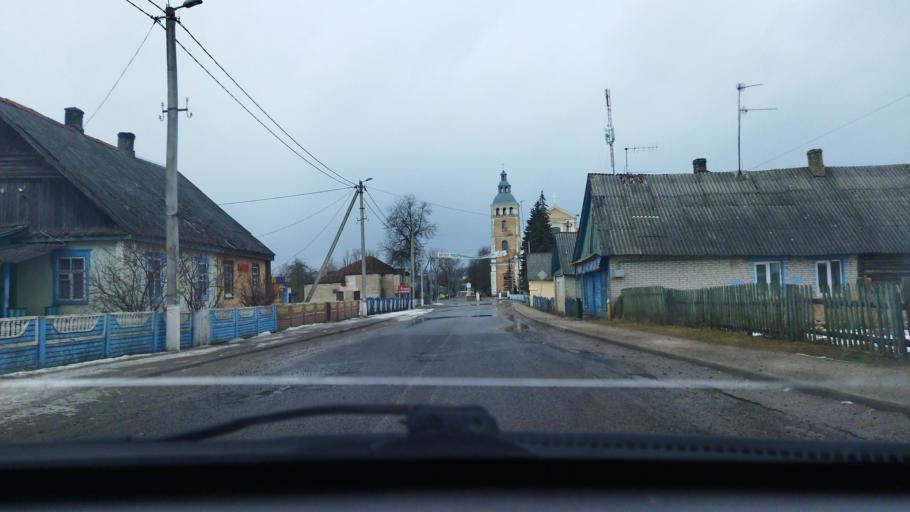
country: BY
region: Minsk
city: Svir
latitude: 54.8517
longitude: 26.3977
